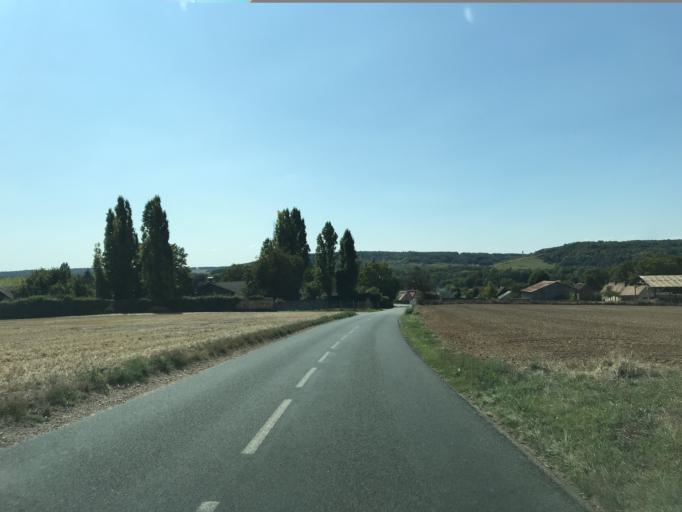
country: FR
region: Haute-Normandie
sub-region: Departement de l'Eure
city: Houlbec-Cocherel
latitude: 49.0783
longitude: 1.3067
